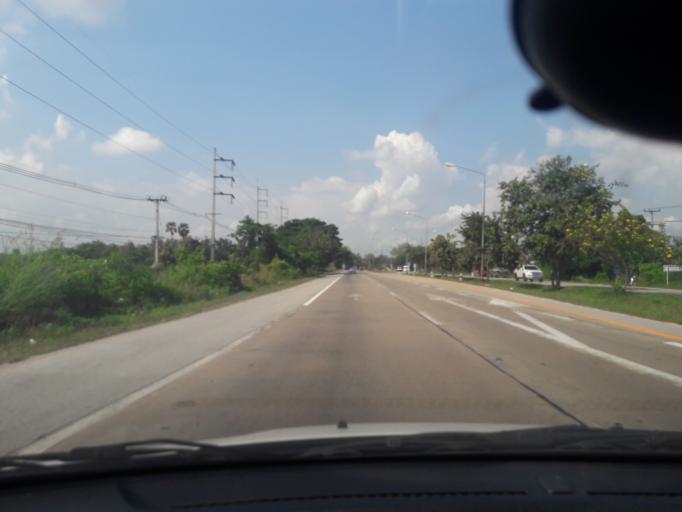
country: TH
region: Lampang
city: Lampang
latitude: 18.2906
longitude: 99.4310
